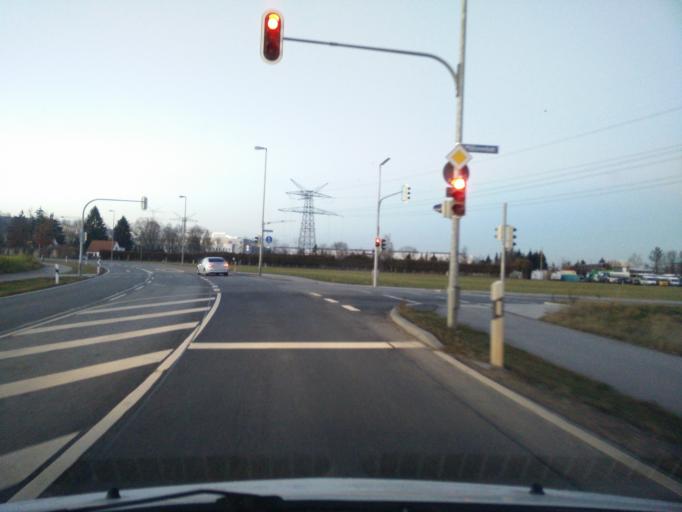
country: DE
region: Bavaria
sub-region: Upper Bavaria
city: Pasing
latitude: 48.1733
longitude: 11.4359
